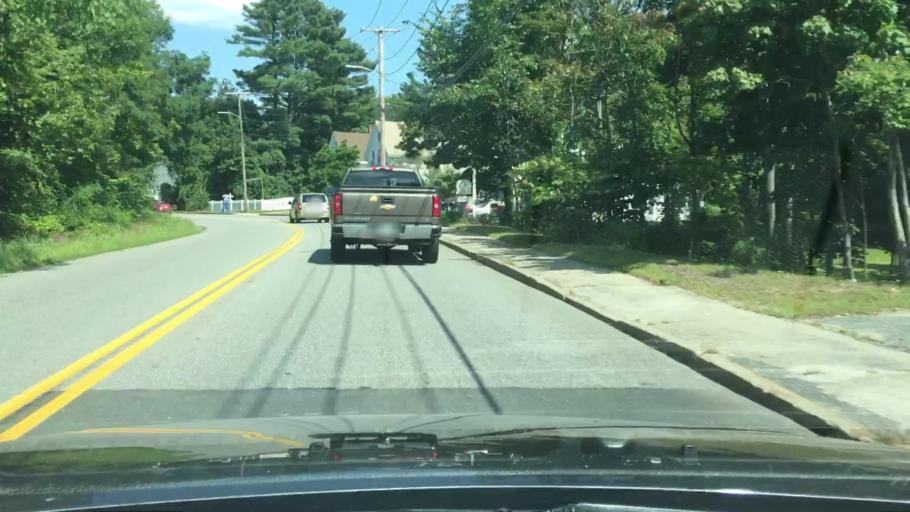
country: US
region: Massachusetts
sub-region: Worcester County
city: Milford
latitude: 42.1561
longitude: -71.5195
